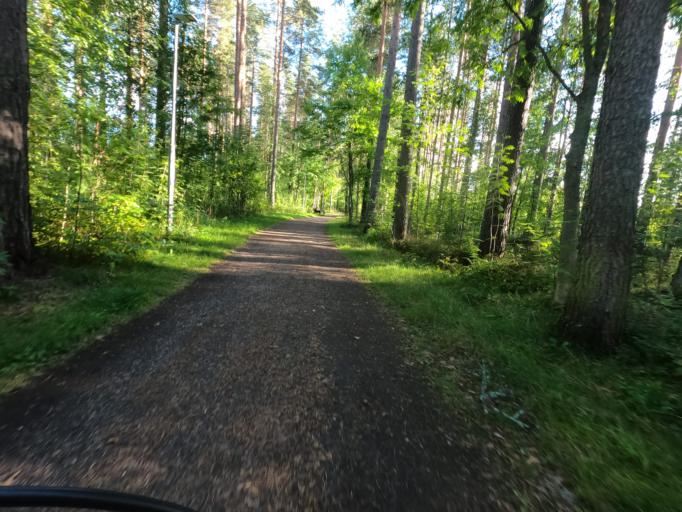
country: FI
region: North Karelia
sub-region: Joensuu
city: Joensuu
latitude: 62.6146
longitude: 29.7525
